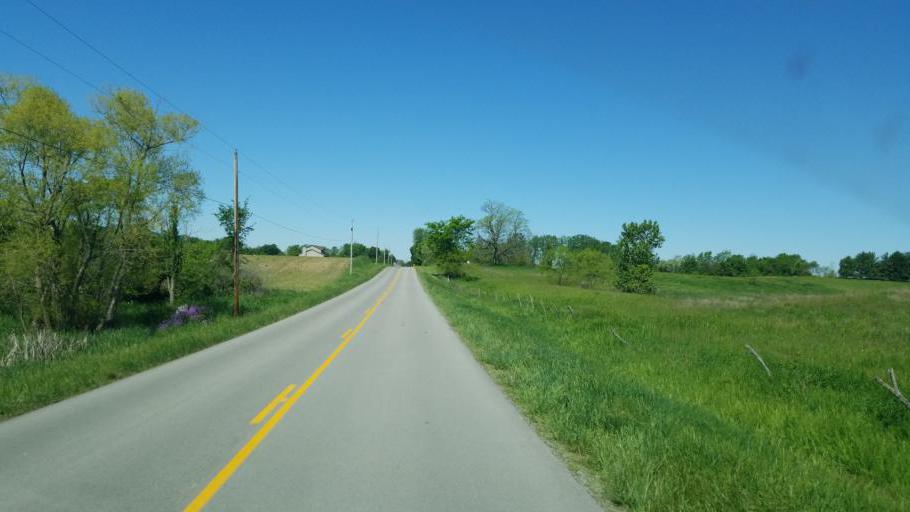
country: US
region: Ohio
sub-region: Logan County
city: Russells Point
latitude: 40.4249
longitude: -83.8752
